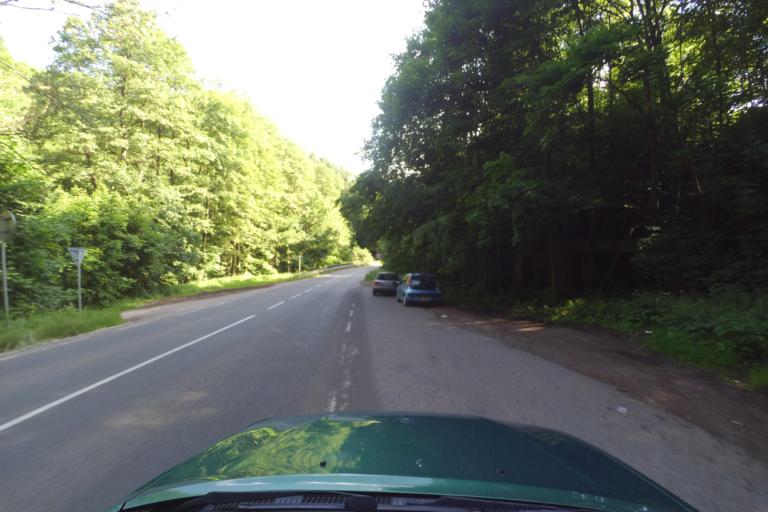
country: CZ
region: Kralovehradecky
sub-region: Okres Trutnov
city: Trutnov
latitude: 50.5999
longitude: 15.9492
